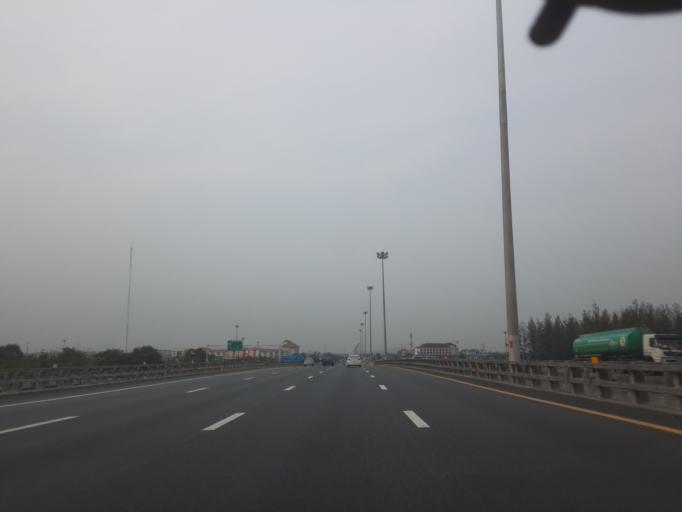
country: TH
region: Chon Buri
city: Chon Buri
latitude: 13.4067
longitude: 101.0472
